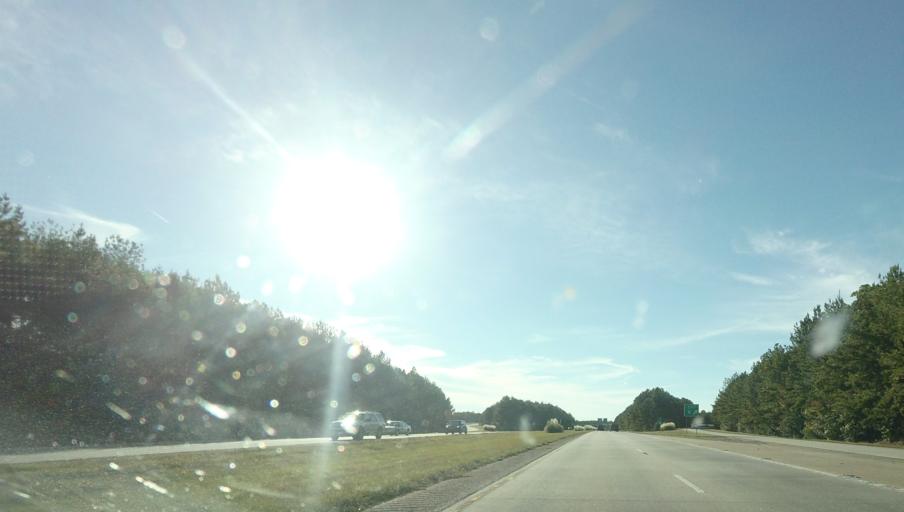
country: US
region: Georgia
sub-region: Muscogee County
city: Columbus
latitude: 32.5551
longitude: -84.8926
